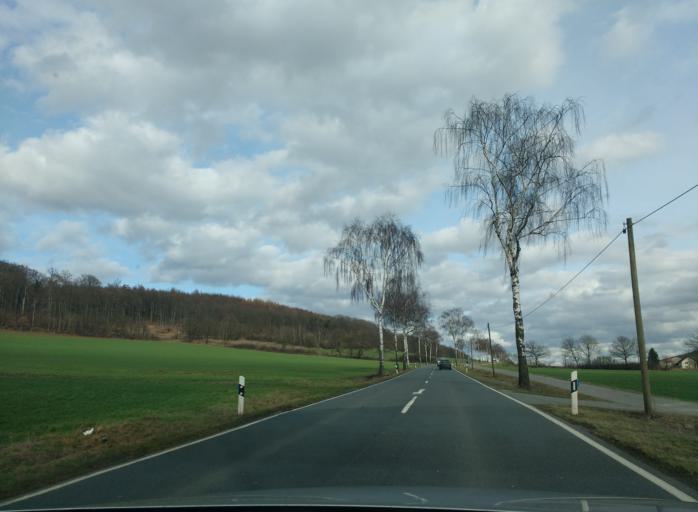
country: DE
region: Lower Saxony
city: Rinteln
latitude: 52.1541
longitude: 8.9806
